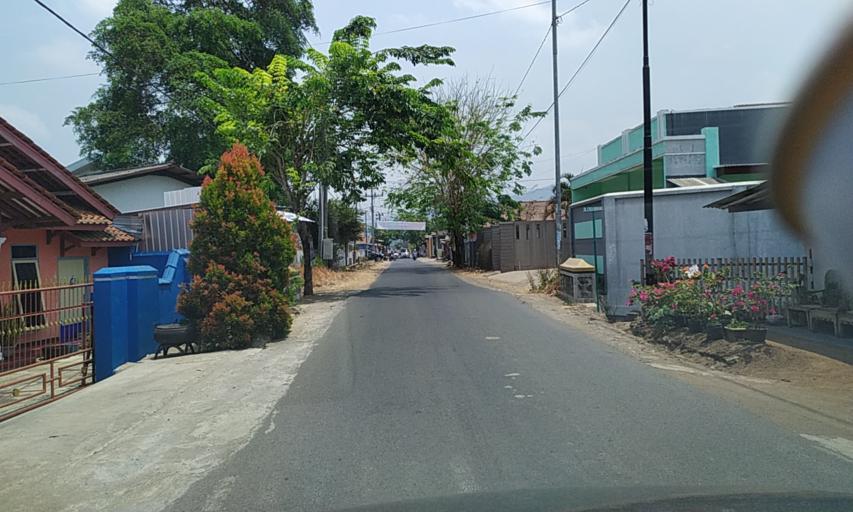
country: ID
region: Central Java
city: Jenang Selatan
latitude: -7.2982
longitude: 108.7566
